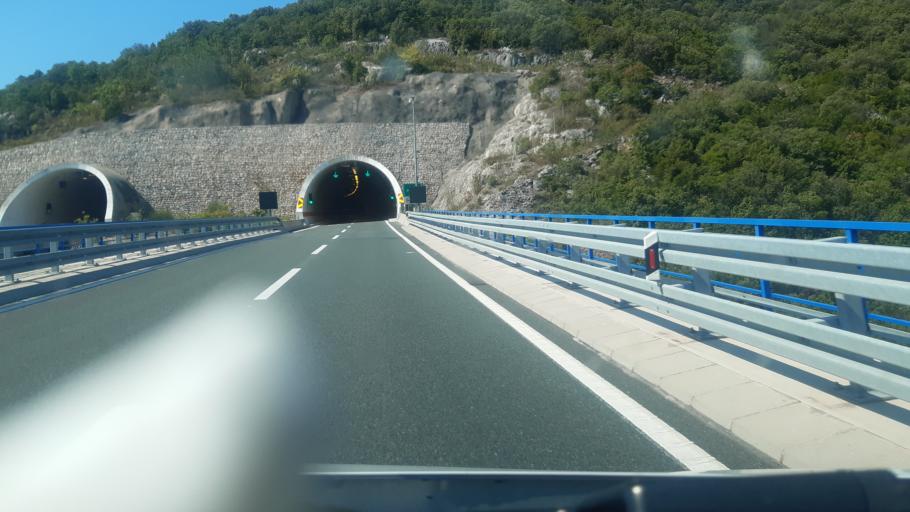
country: HR
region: Dubrovacko-Neretvanska
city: Komin
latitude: 43.1164
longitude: 17.4815
